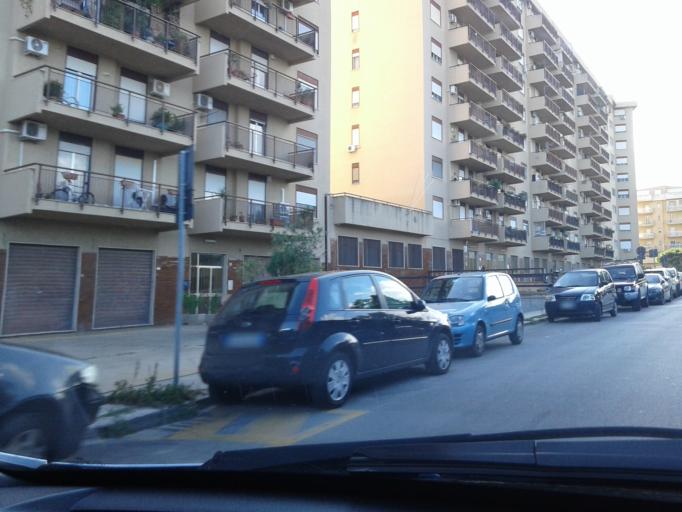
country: IT
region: Sicily
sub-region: Palermo
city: Palermo
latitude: 38.1033
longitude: 13.3232
